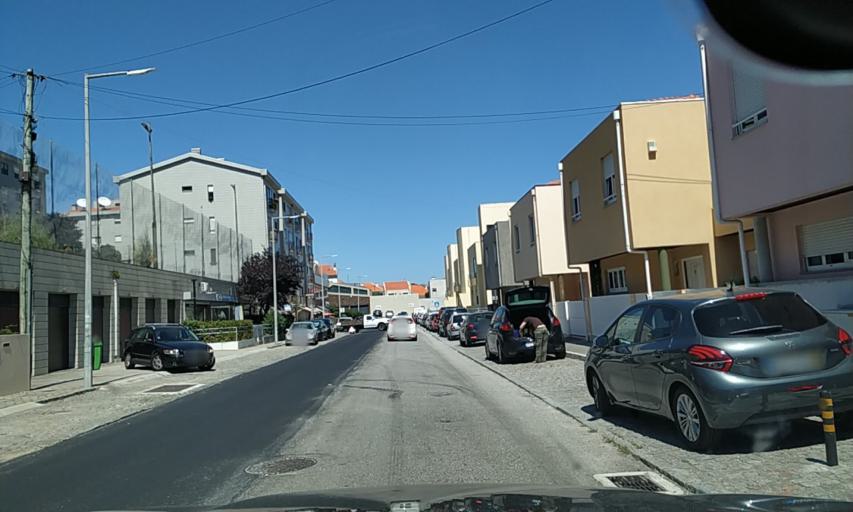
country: PT
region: Porto
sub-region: Vila Nova de Gaia
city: Canidelo
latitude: 41.1363
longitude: -8.6433
